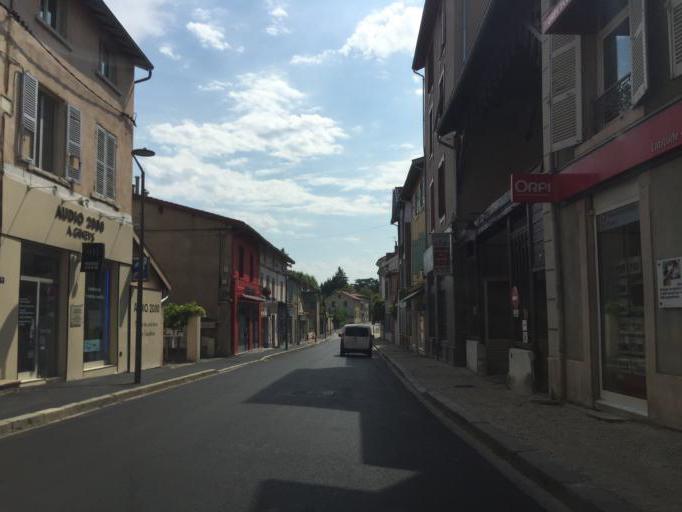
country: FR
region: Rhone-Alpes
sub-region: Departement du Rhone
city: Ecully
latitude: 45.7742
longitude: 4.7787
